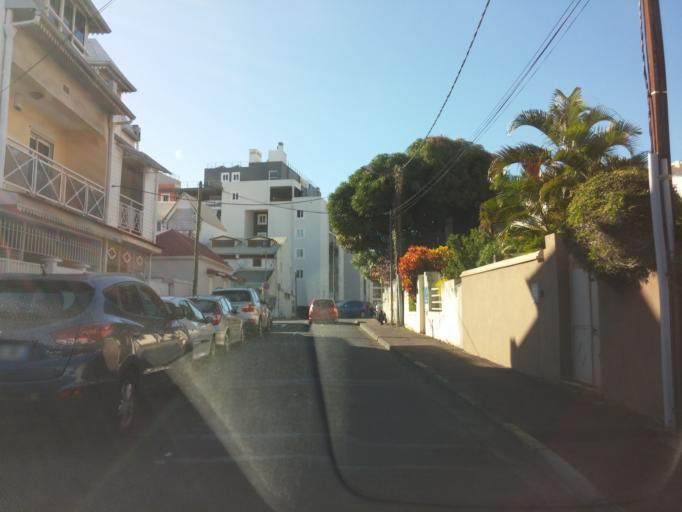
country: RE
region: Reunion
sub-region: Reunion
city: Saint-Denis
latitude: -20.8819
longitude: 55.4589
